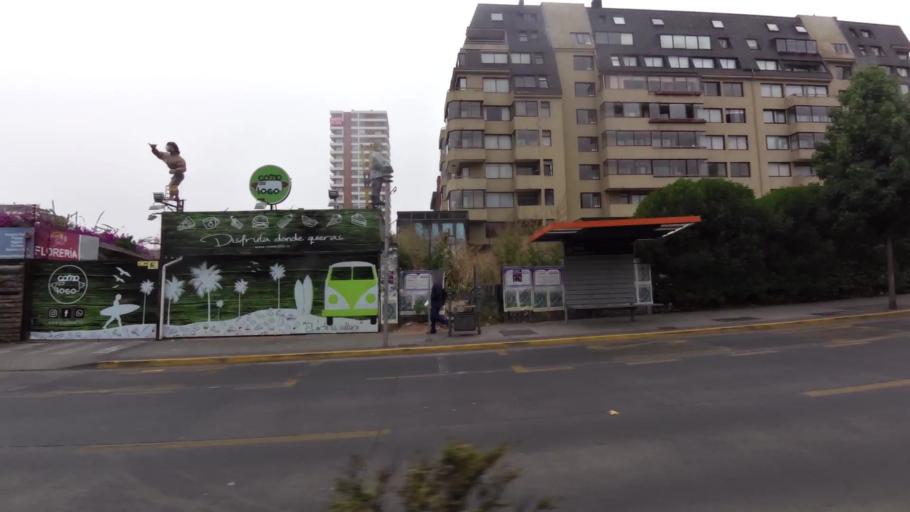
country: CL
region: Biobio
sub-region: Provincia de Concepcion
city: Concepcion
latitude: -36.8226
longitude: -73.0426
